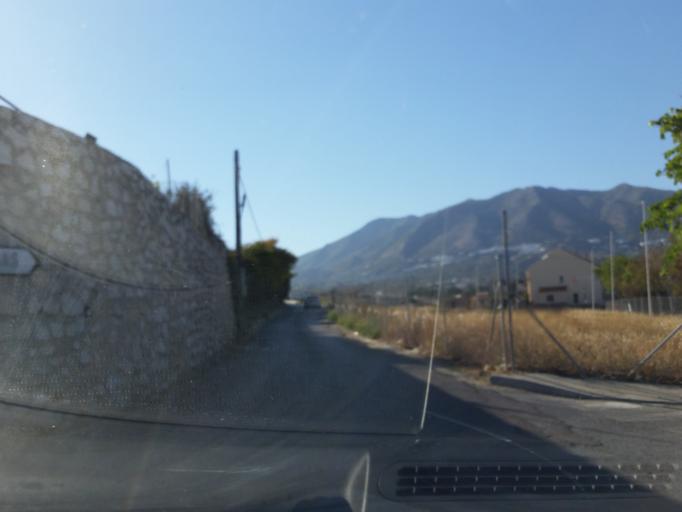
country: ES
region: Andalusia
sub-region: Provincia de Malaga
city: Fuengirola
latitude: 36.5592
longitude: -4.6210
